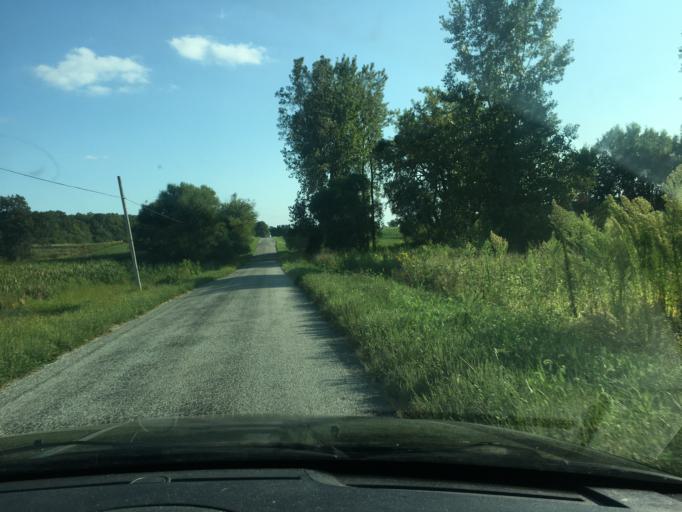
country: US
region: Ohio
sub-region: Logan County
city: West Liberty
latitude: 40.2447
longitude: -83.7854
